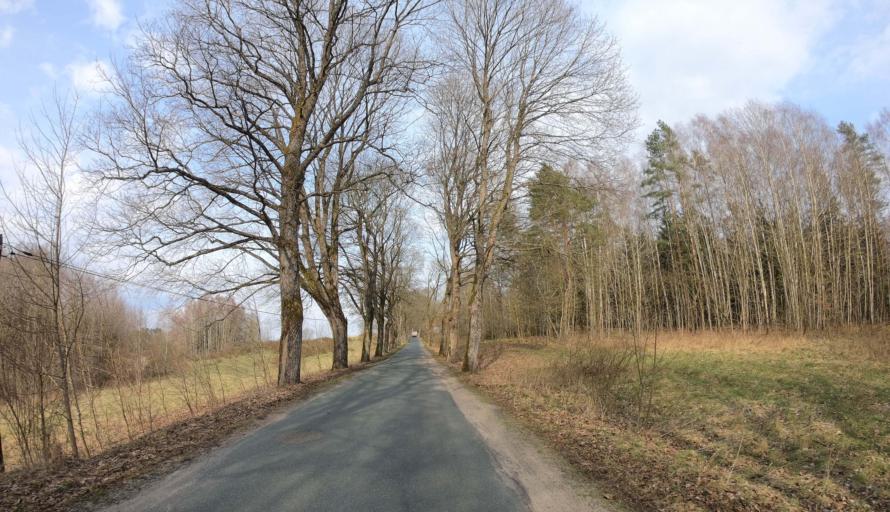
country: PL
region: West Pomeranian Voivodeship
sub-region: Powiat swidwinski
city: Swidwin
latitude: 53.8258
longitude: 15.8237
